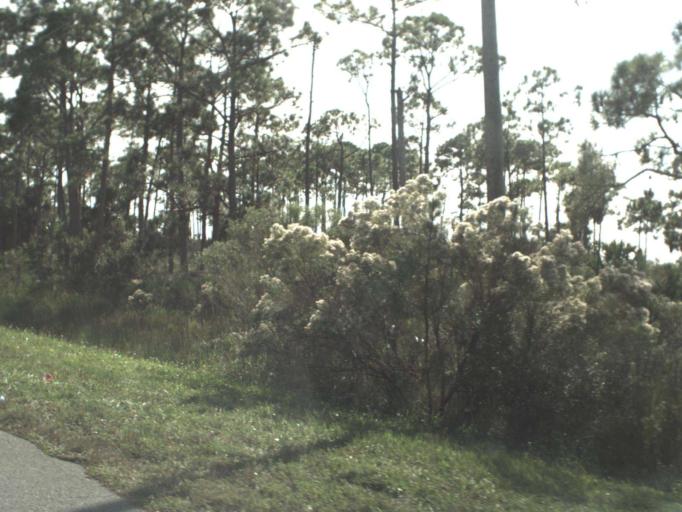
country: US
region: Florida
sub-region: Gulf County
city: Port Saint Joe
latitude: 29.7857
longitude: -85.3013
